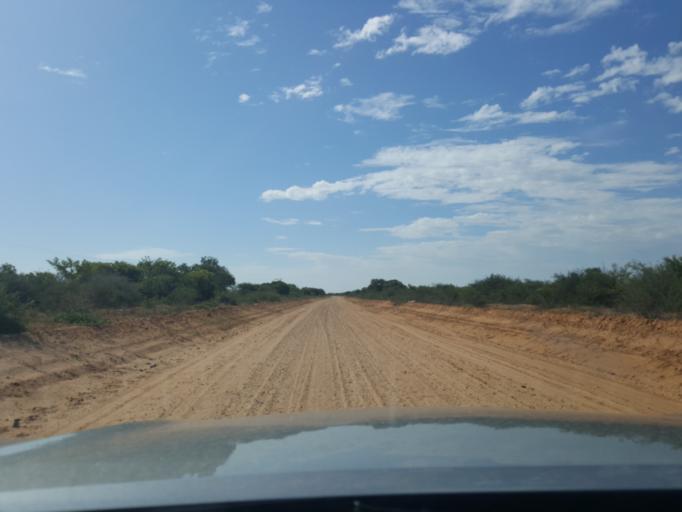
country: BW
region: Kweneng
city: Khudumelapye
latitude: -23.7494
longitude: 24.7544
